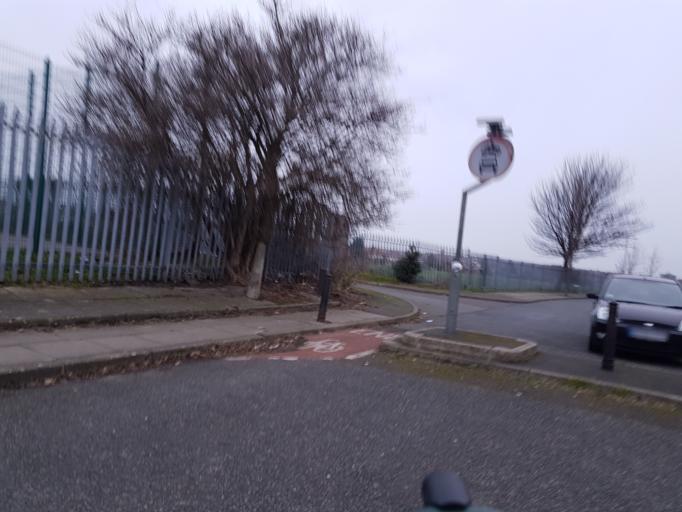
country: GB
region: England
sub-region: Sefton
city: Litherland
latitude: 53.4493
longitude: -2.9736
